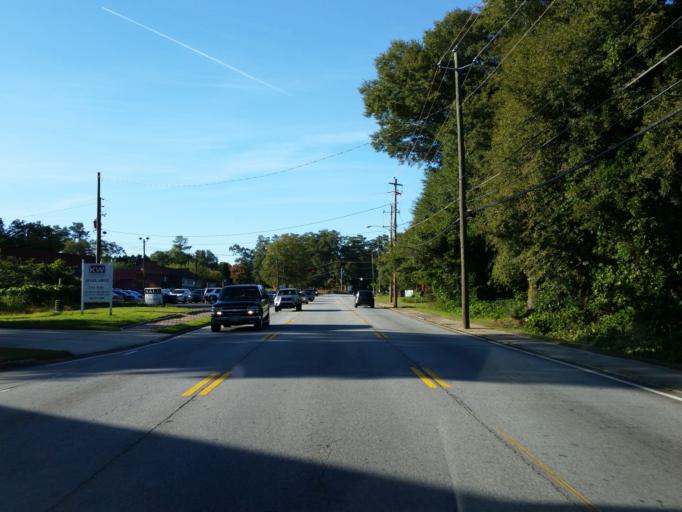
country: US
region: Georgia
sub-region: Fulton County
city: Roswell
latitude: 34.0099
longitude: -84.3614
